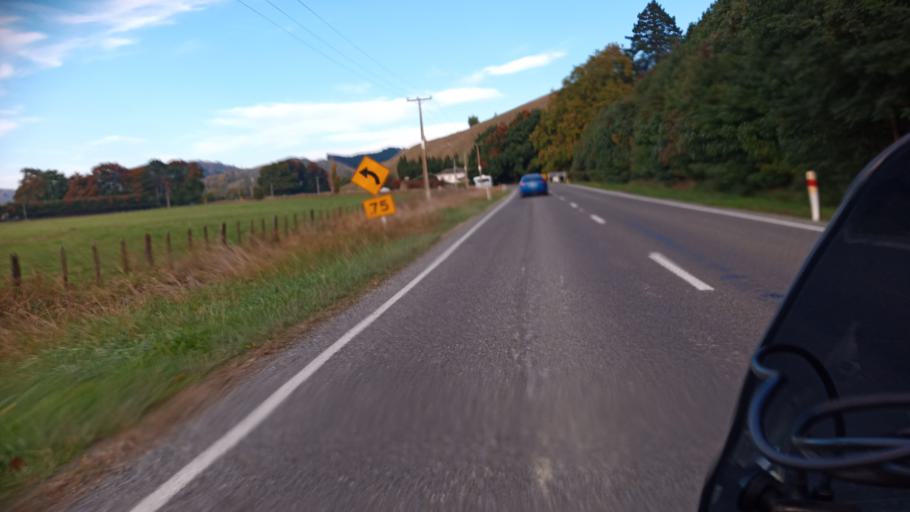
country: NZ
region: Gisborne
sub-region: Gisborne District
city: Gisborne
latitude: -38.7581
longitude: 177.9188
